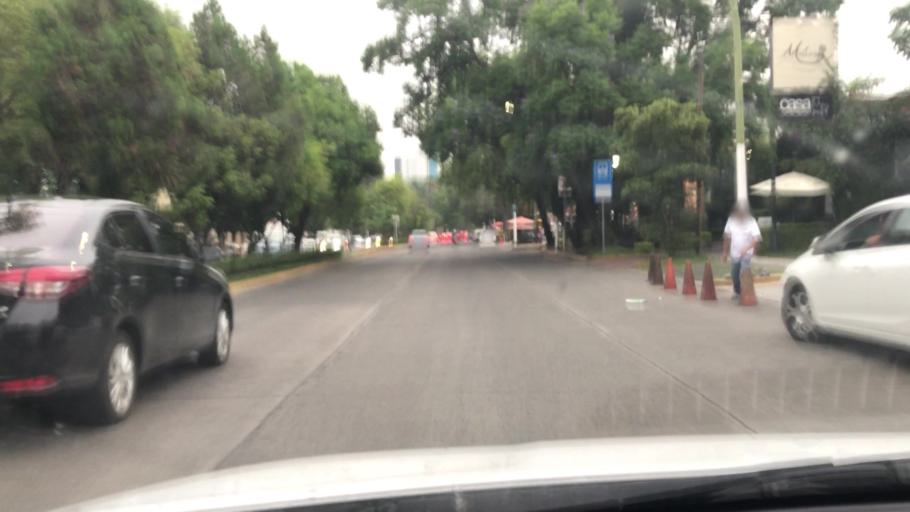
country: MX
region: Jalisco
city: Guadalajara
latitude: 20.6658
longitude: -103.4053
